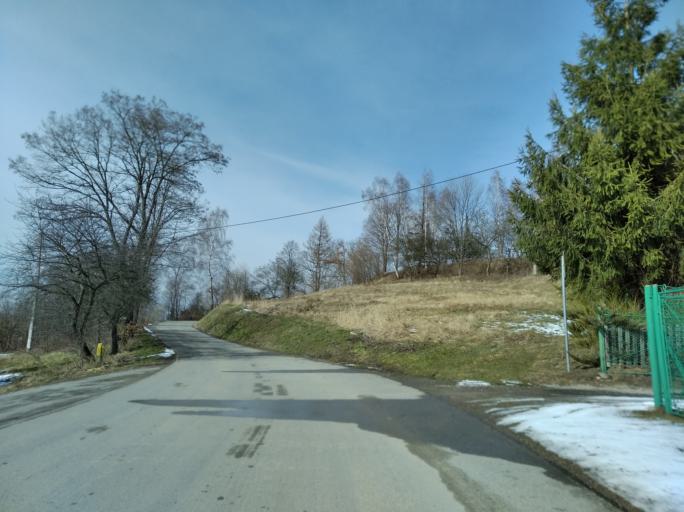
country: PL
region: Subcarpathian Voivodeship
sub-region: Powiat krosnienski
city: Korczyna
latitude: 49.7384
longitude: 21.7857
